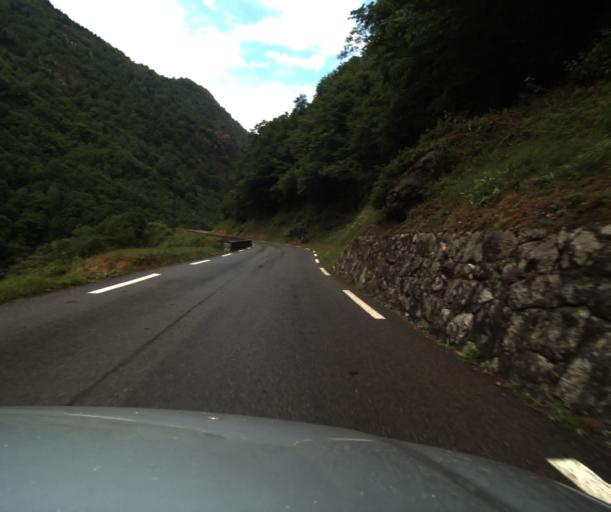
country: FR
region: Midi-Pyrenees
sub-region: Departement des Hautes-Pyrenees
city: Luz-Saint-Sauveur
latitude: 42.8424
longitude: -0.0062
